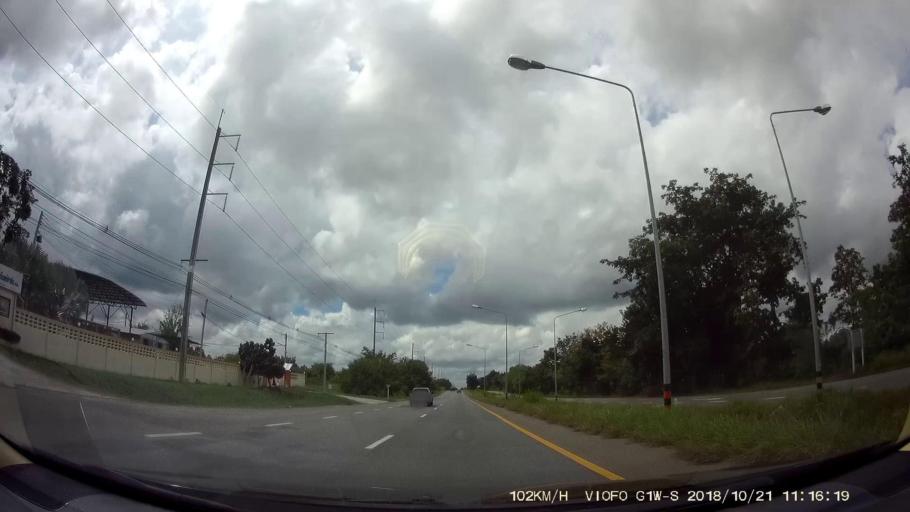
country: TH
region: Chaiyaphum
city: Chaiyaphum
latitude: 15.8864
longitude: 102.1044
